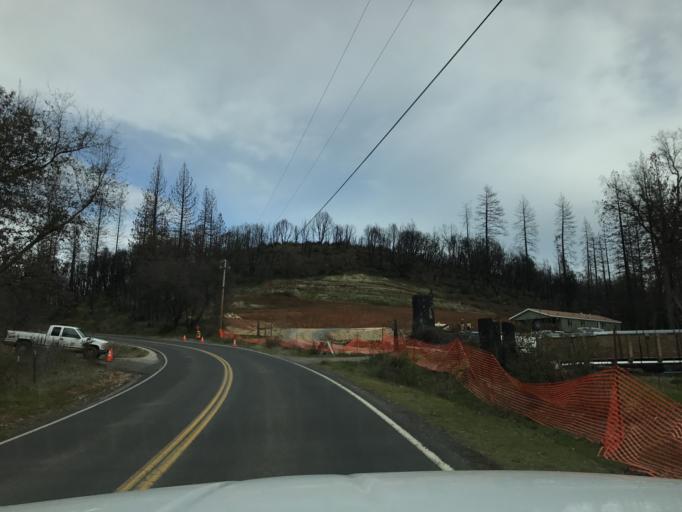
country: US
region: California
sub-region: Calaveras County
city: Mountain Ranch
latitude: 38.2365
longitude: -120.5209
